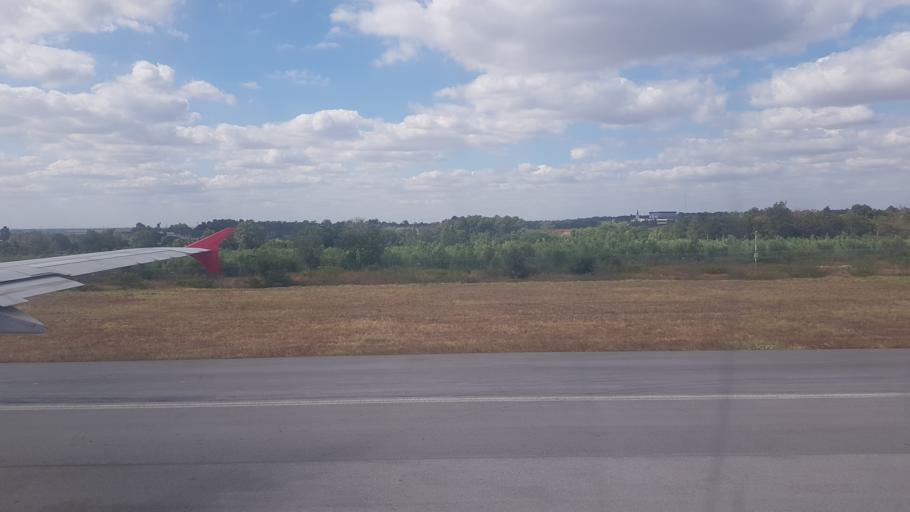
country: TH
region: Khon Kaen
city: Khon Kaen
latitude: 16.4622
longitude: 102.7808
